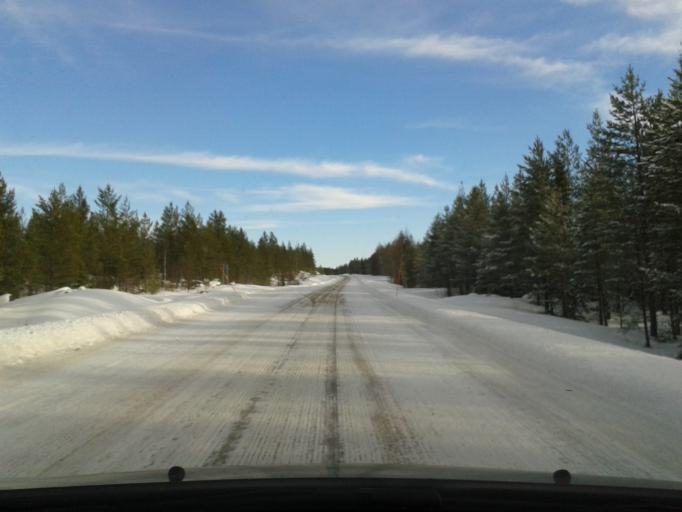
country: SE
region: Vaesterbotten
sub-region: Asele Kommun
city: Asele
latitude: 64.3163
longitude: 17.1633
